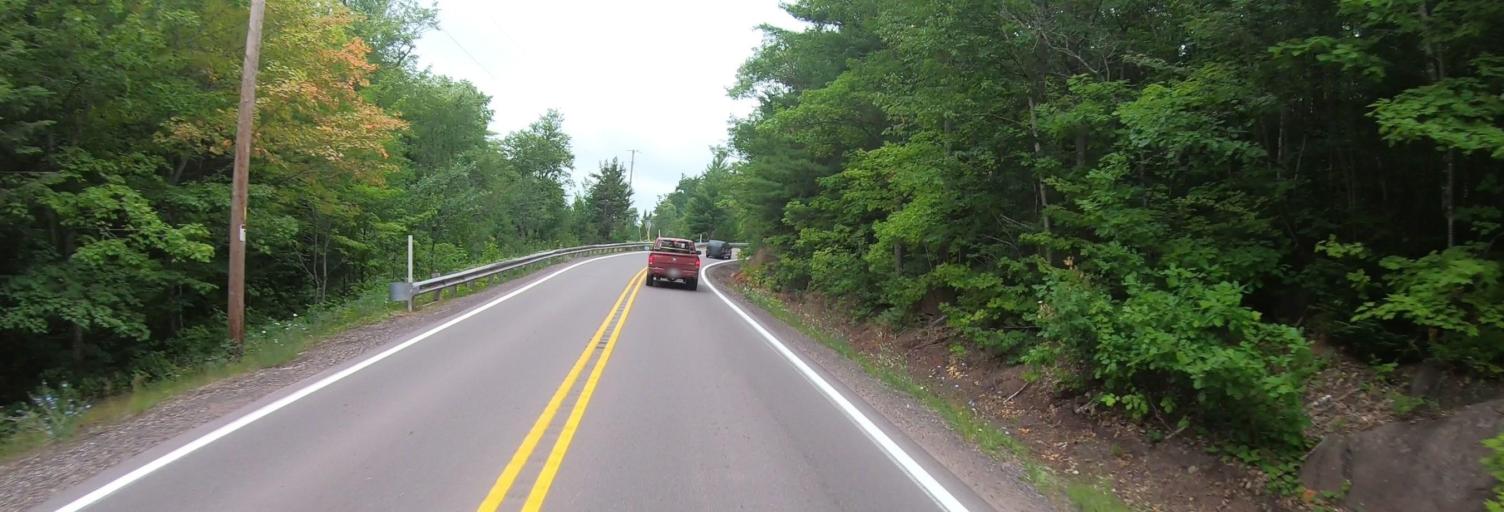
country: US
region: Michigan
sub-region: Keweenaw County
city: Eagle River
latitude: 47.4309
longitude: -87.9827
